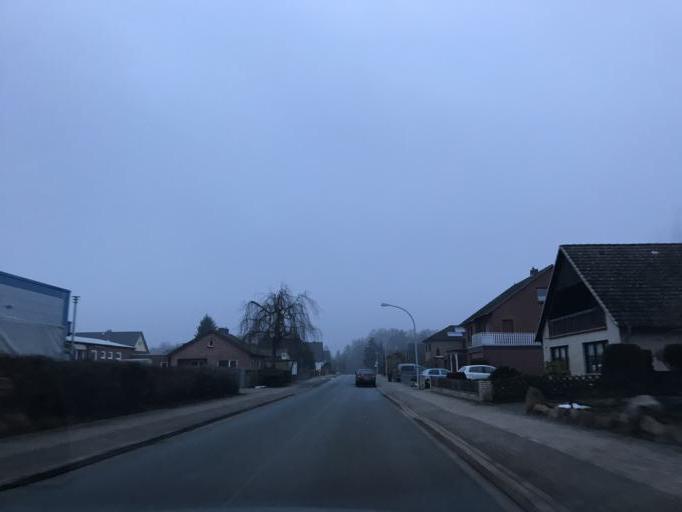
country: DE
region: Lower Saxony
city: Munster
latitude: 52.9948
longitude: 10.1048
